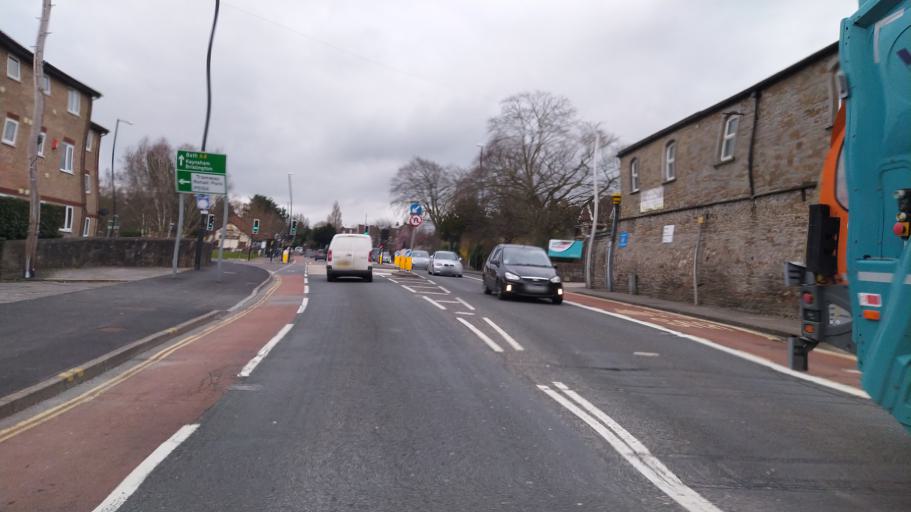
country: GB
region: England
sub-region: Bath and North East Somerset
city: Whitchurch
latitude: 51.4382
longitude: -2.5578
